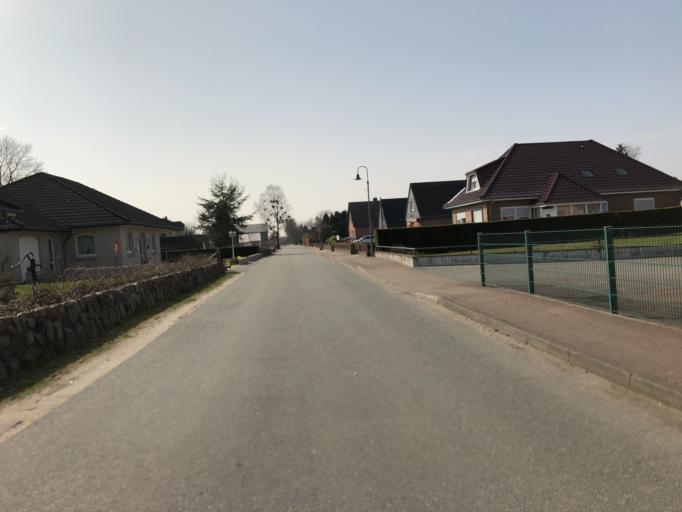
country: DE
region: Schleswig-Holstein
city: Jerrishoe
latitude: 54.6579
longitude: 9.3716
